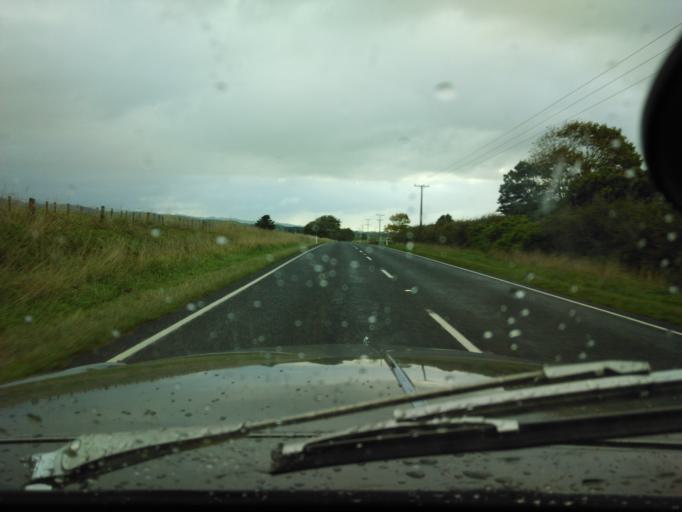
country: NZ
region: Waikato
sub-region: Hauraki District
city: Paeroa
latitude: -37.5859
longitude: 175.5019
